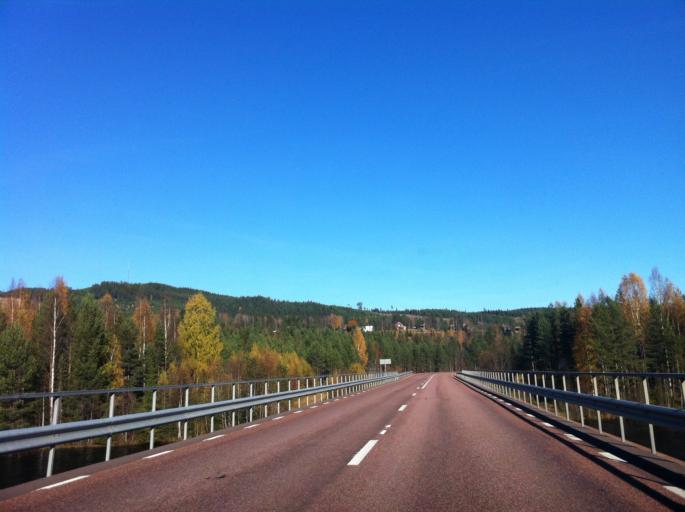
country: SE
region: Dalarna
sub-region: Alvdalens Kommun
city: AElvdalen
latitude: 61.2774
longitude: 13.9313
